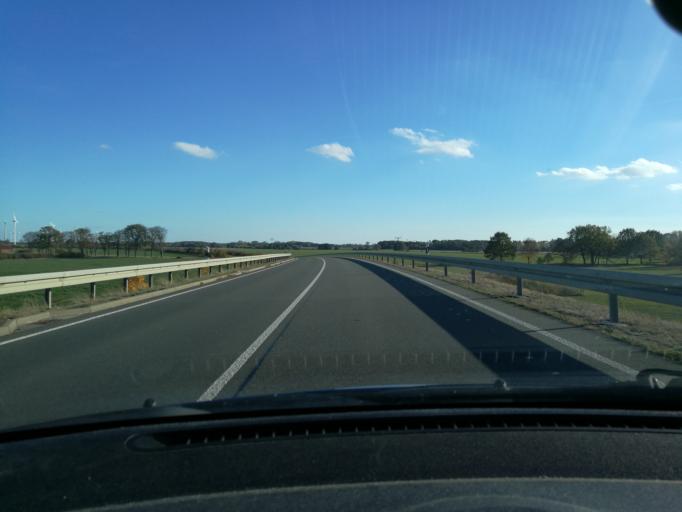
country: DE
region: Brandenburg
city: Karstadt
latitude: 53.1470
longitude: 11.7412
